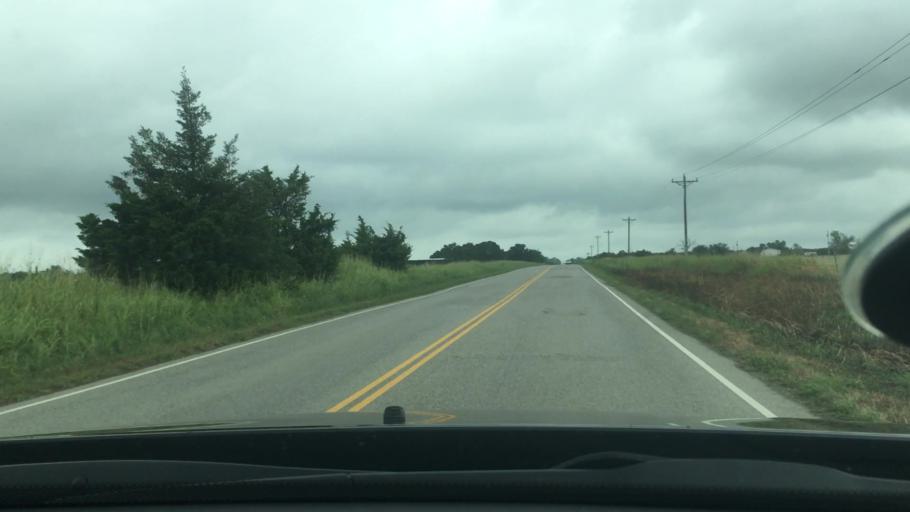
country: US
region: Oklahoma
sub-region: Bryan County
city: Calera
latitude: 33.9336
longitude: -96.5005
